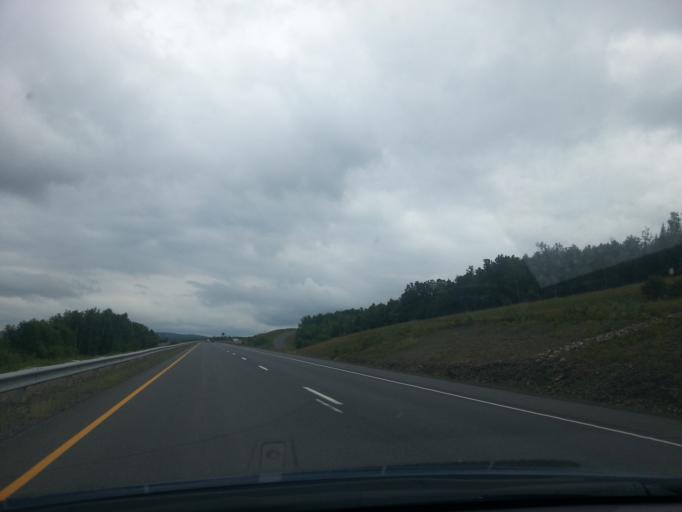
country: US
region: Maine
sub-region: Aroostook County
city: Limestone
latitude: 46.9933
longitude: -67.7269
